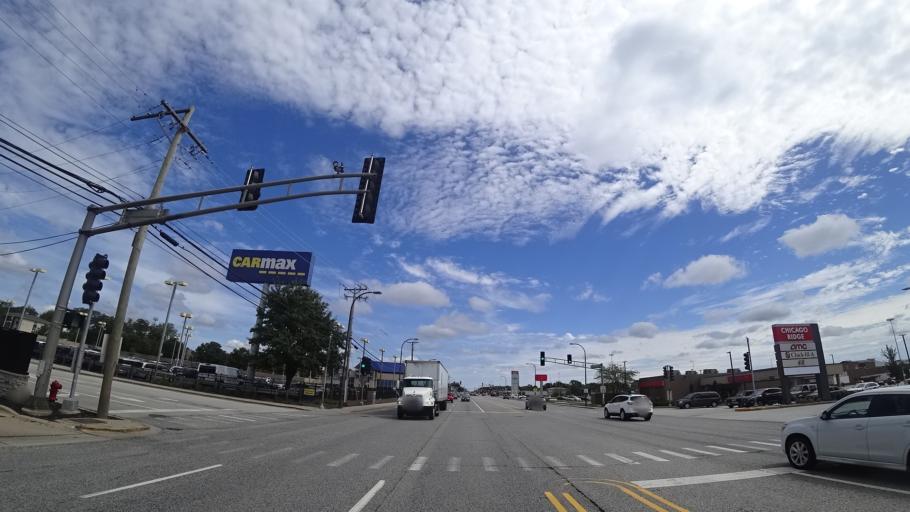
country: US
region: Illinois
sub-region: Cook County
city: Burbank
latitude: 41.7195
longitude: -87.7849
